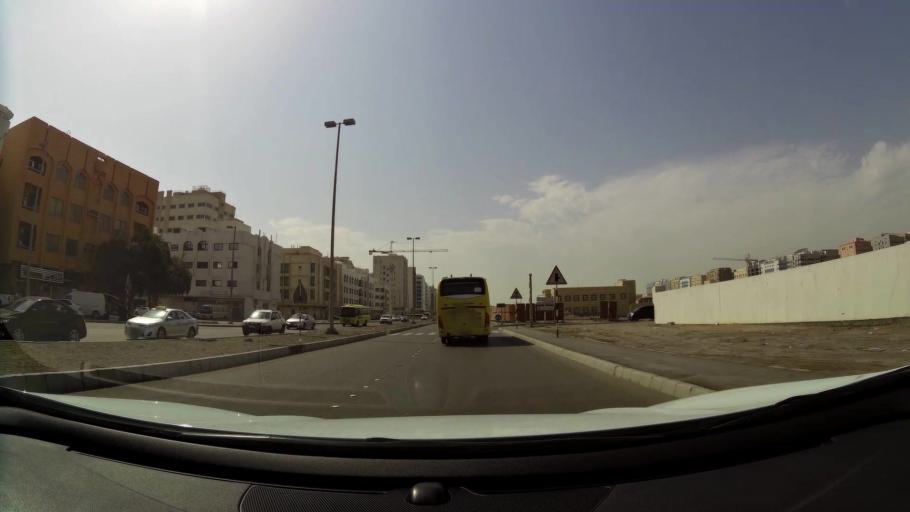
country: AE
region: Abu Dhabi
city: Abu Dhabi
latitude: 24.3382
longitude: 54.5369
